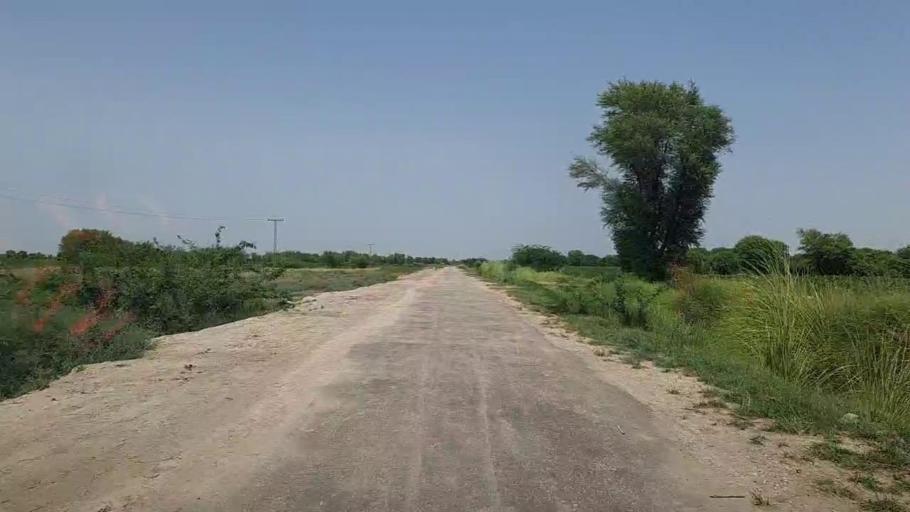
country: PK
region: Sindh
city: Pad Idan
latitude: 26.7467
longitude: 68.3147
